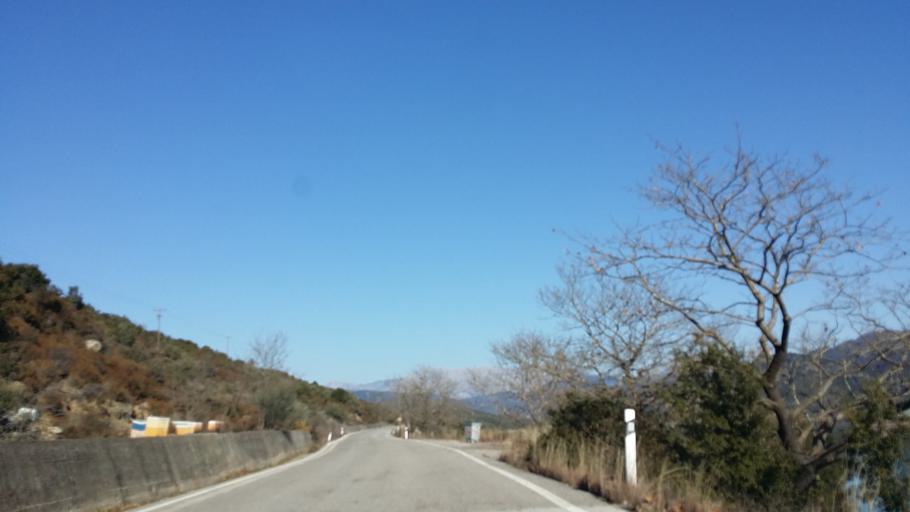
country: GR
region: West Greece
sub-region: Nomos Aitolias kai Akarnanias
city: Lepenou
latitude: 38.8150
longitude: 21.3346
